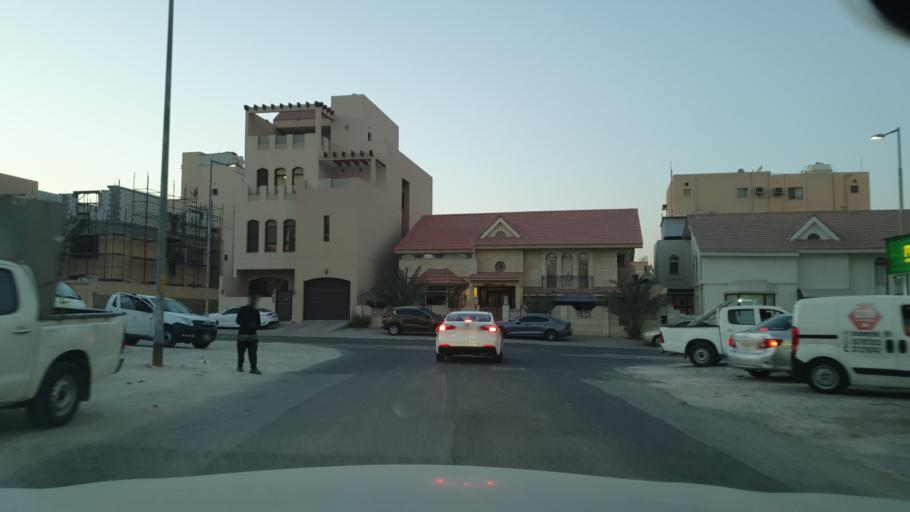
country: BH
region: Northern
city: Ar Rifa'
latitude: 26.1221
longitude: 50.5851
